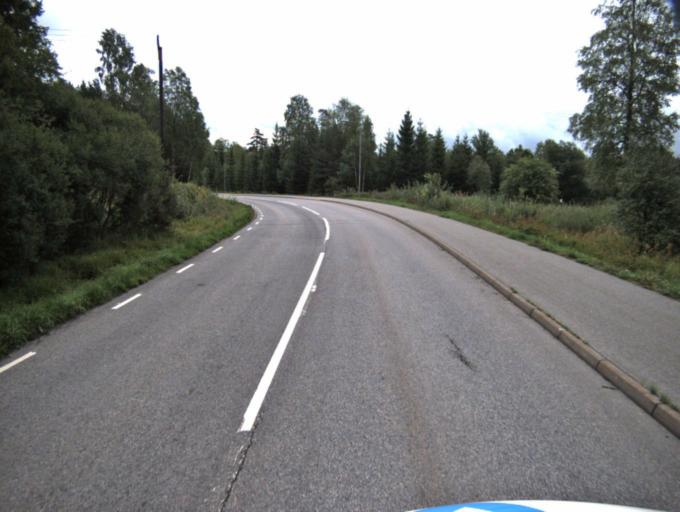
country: SE
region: Vaestra Goetaland
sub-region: Ulricehamns Kommun
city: Ulricehamn
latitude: 57.7700
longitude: 13.4460
